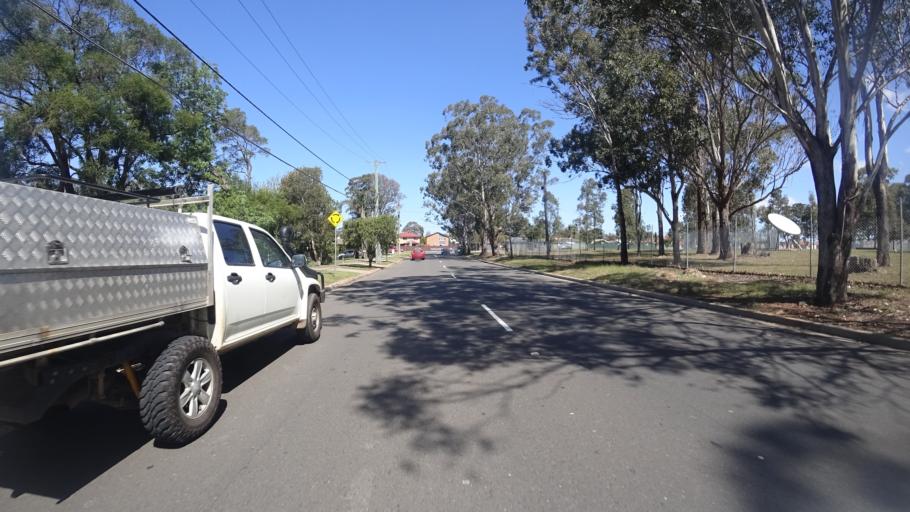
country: AU
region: New South Wales
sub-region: Liverpool
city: Miller
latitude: -33.9440
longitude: 150.8882
